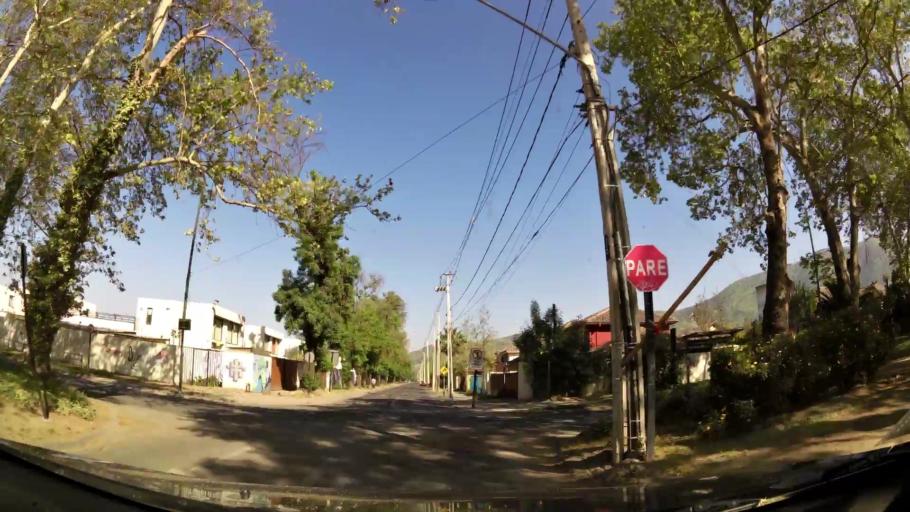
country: CL
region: Santiago Metropolitan
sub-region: Provincia de Chacabuco
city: Chicureo Abajo
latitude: -33.3493
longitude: -70.6706
